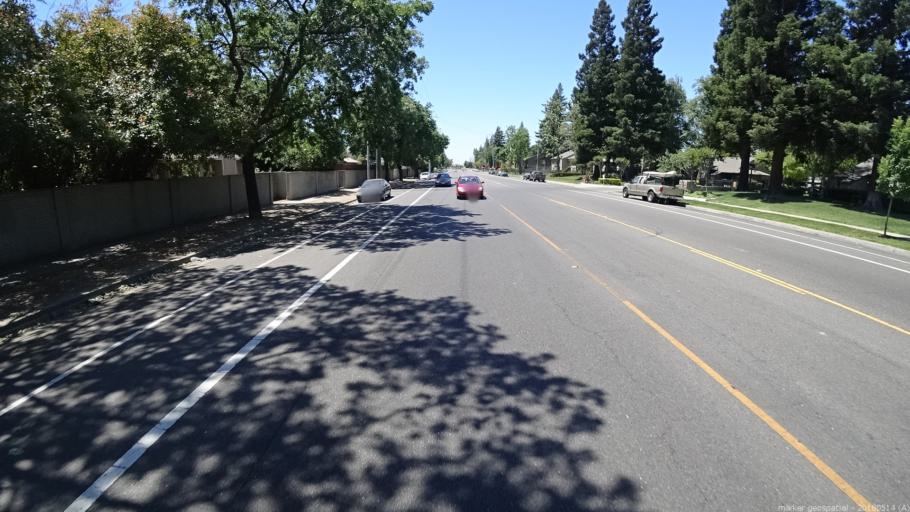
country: US
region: California
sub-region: Sacramento County
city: Sacramento
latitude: 38.6274
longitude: -121.5039
